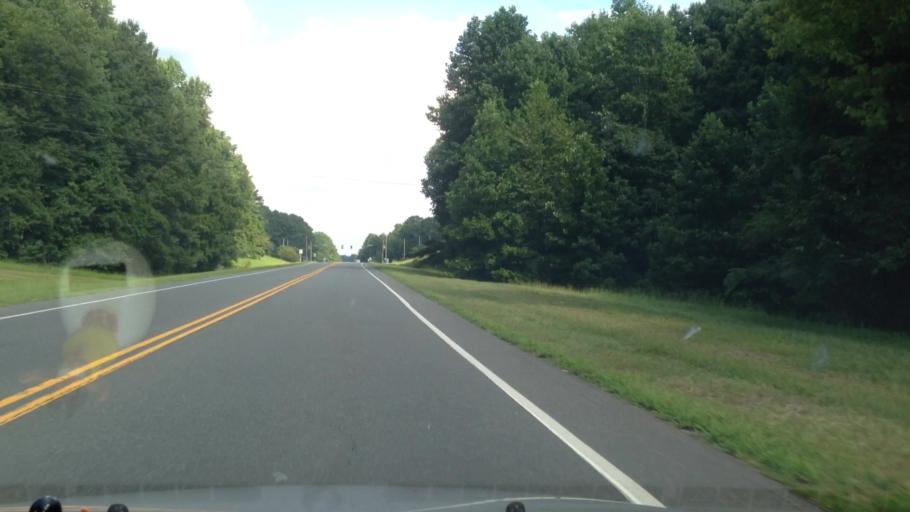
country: US
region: North Carolina
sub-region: Lee County
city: Broadway
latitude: 35.4455
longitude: -79.1137
